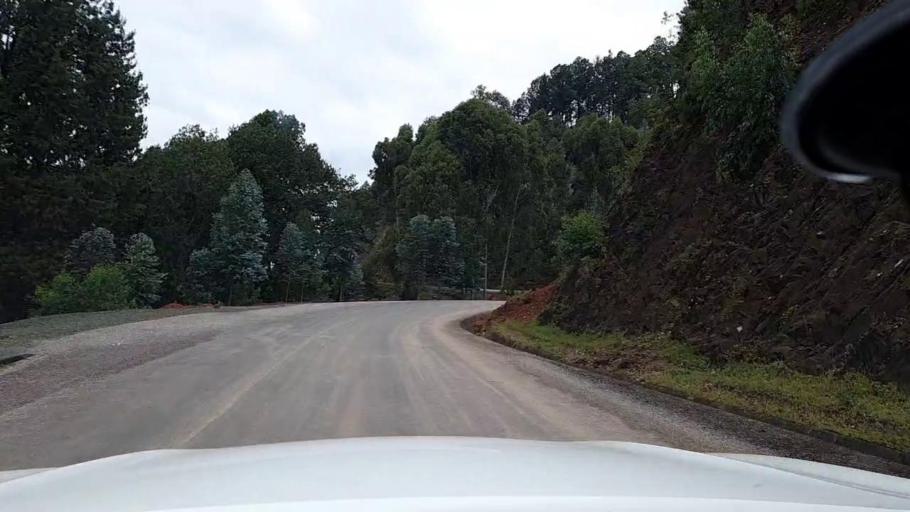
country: RW
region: Southern Province
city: Gitarama
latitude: -2.0642
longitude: 29.5587
